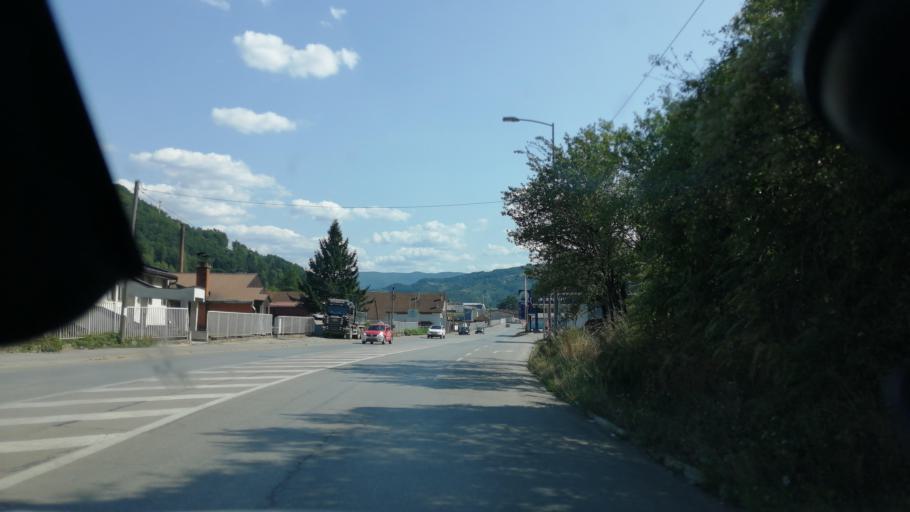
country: RS
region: Central Serbia
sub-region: Moravicki Okrug
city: Ivanjica
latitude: 43.5943
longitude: 20.2224
